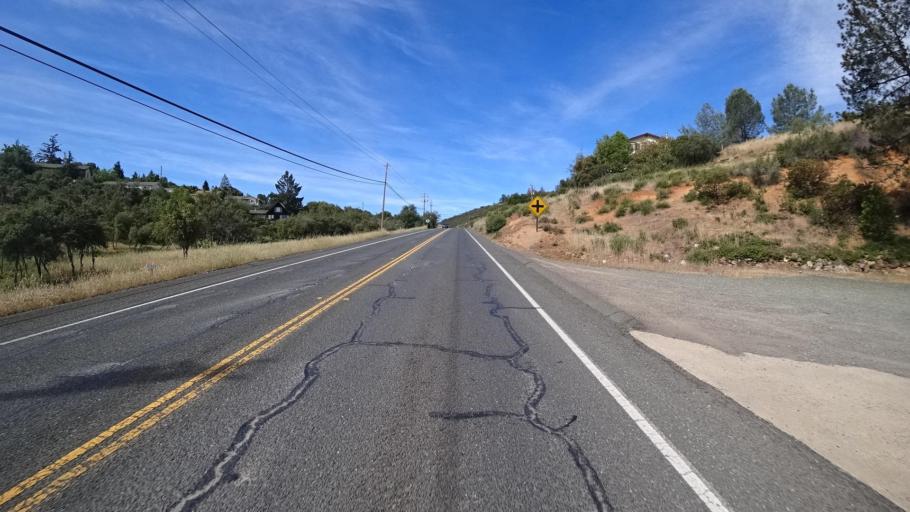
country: US
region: California
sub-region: Lake County
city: Soda Bay
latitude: 38.9520
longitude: -122.7301
